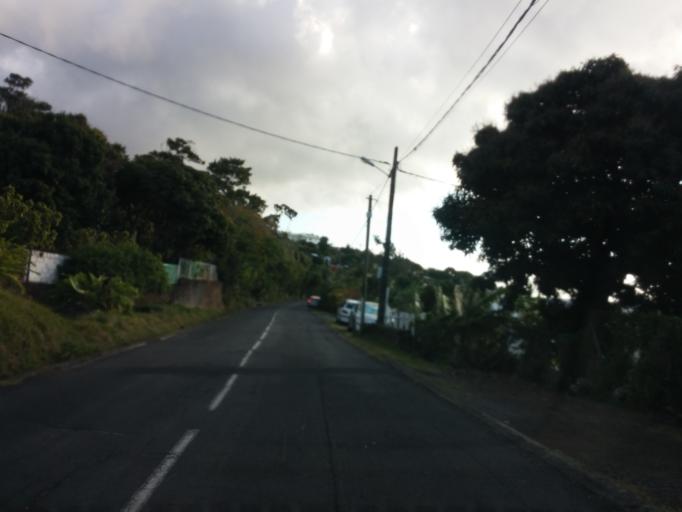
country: RE
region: Reunion
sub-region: Reunion
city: Saint-Denis
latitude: -20.8850
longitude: 55.4243
